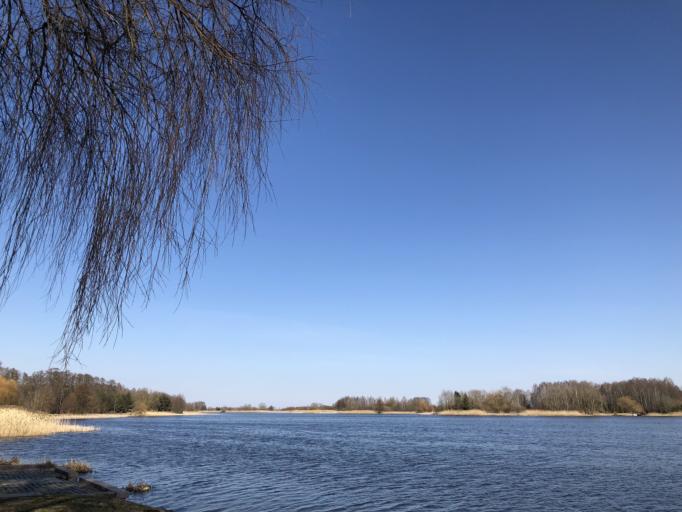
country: BY
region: Minsk
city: Nyasvizh
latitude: 53.2277
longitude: 26.6977
